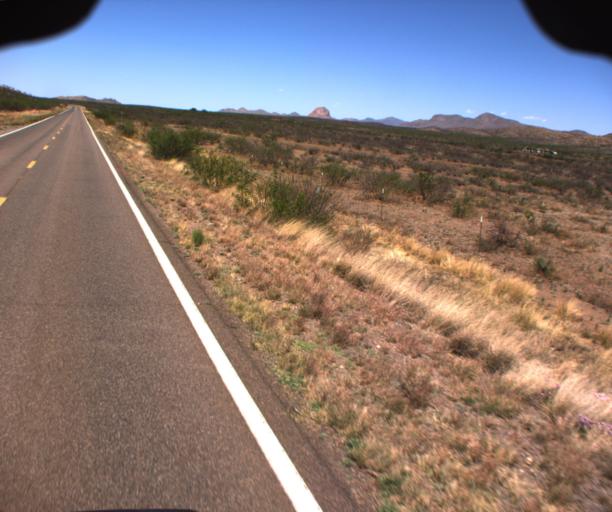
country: US
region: Arizona
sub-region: Cochise County
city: Douglas
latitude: 31.4877
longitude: -109.4188
